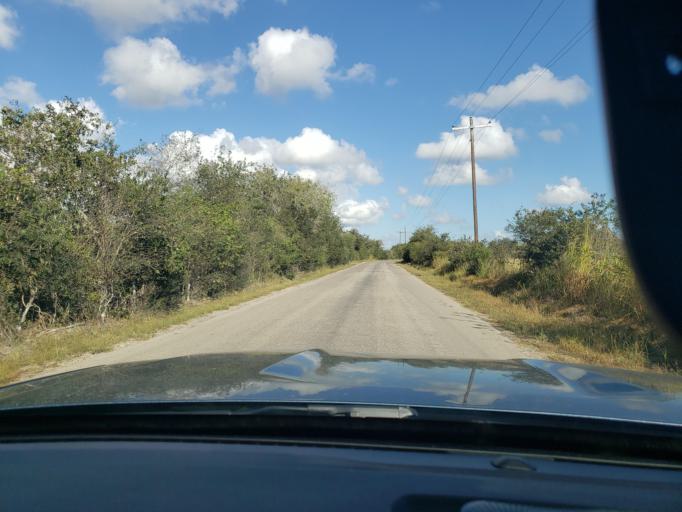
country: US
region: Texas
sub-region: Bee County
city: Beeville
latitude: 28.4460
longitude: -97.7160
